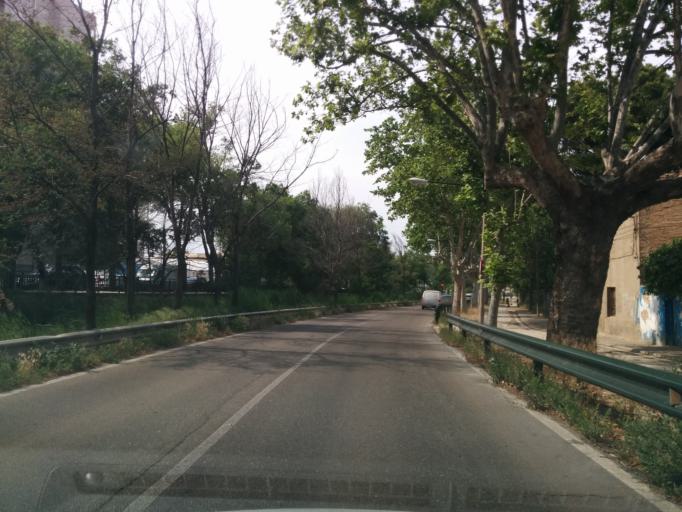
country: ES
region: Aragon
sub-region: Provincia de Zaragoza
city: Zaragoza
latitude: 41.6314
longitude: -0.8813
